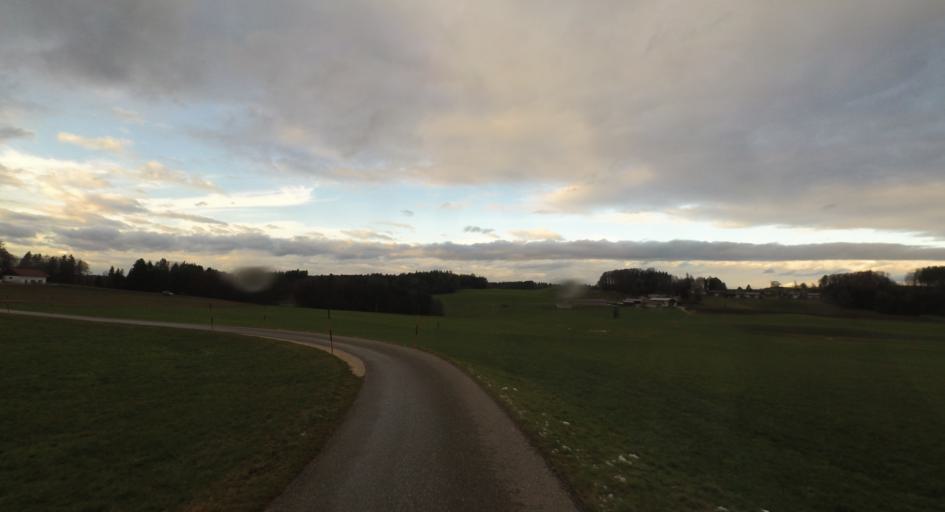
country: DE
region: Bavaria
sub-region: Upper Bavaria
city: Vachendorf
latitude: 47.8530
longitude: 12.6024
